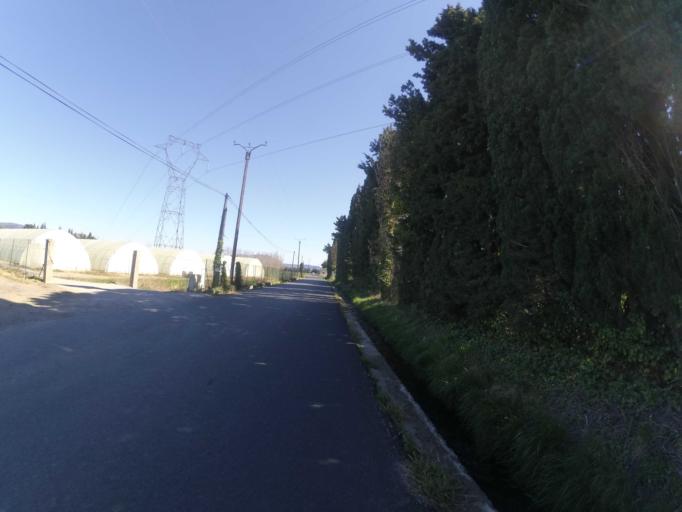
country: FR
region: Languedoc-Roussillon
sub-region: Departement des Pyrenees-Orientales
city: Ille-sur-Tet
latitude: 42.6653
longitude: 2.6383
